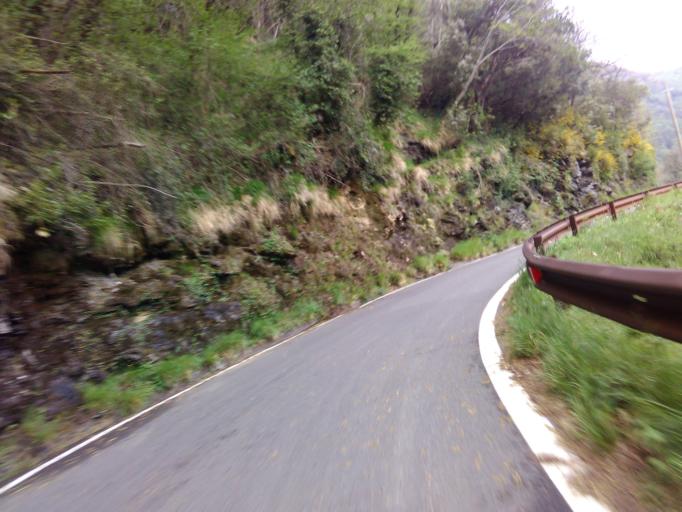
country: IT
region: Tuscany
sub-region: Provincia di Lucca
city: Pontestazzemese
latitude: 43.9748
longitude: 10.2765
